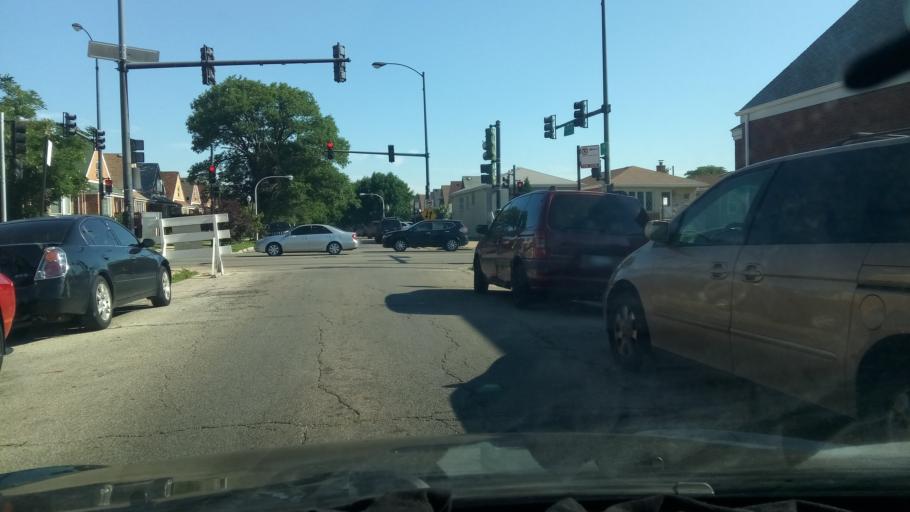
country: US
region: Illinois
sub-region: Cook County
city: Hometown
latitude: 41.7705
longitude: -87.7322
